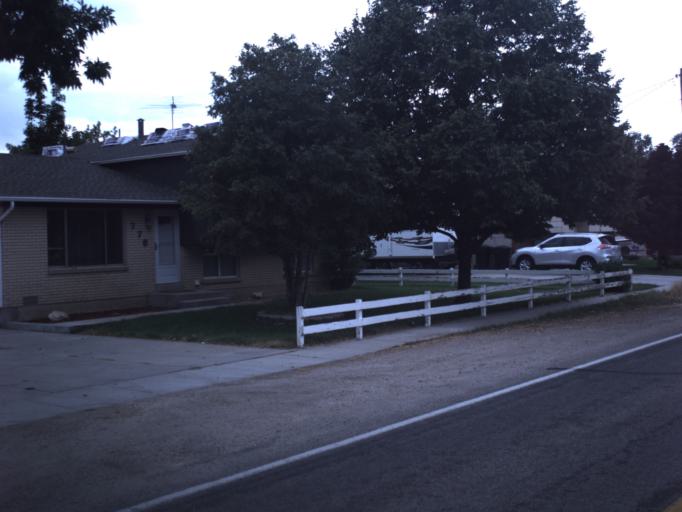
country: US
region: Utah
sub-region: Davis County
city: West Point
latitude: 41.1249
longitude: -112.1126
